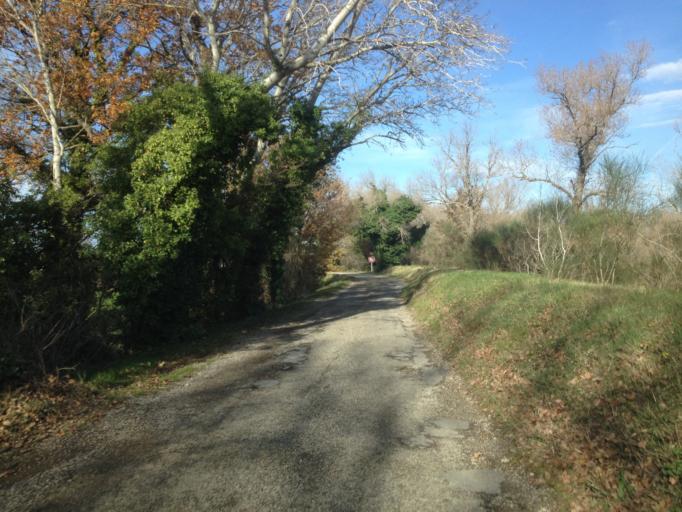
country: FR
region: Provence-Alpes-Cote d'Azur
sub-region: Departement du Vaucluse
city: Sarrians
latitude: 44.0712
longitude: 4.9294
